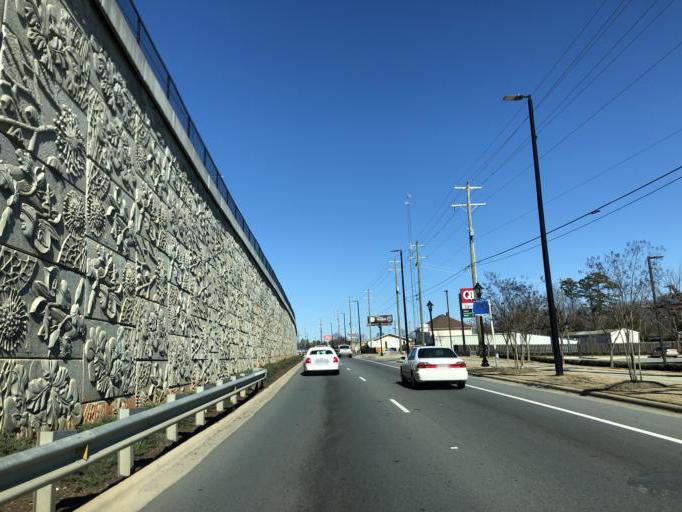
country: US
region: North Carolina
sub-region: Mecklenburg County
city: Charlotte
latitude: 35.2635
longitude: -80.7712
